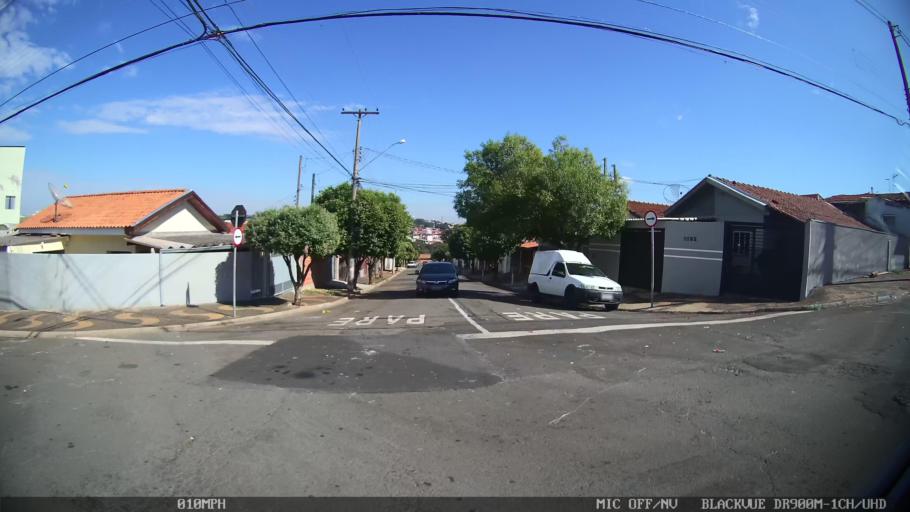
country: BR
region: Sao Paulo
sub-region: Santa Barbara D'Oeste
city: Santa Barbara d'Oeste
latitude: -22.7357
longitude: -47.3886
